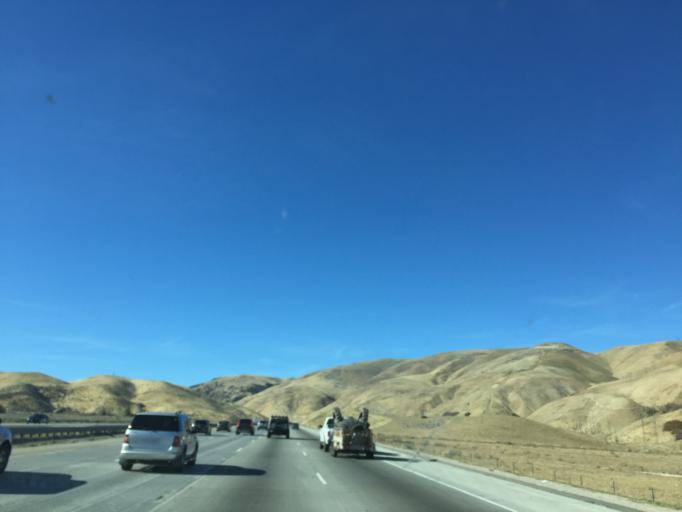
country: US
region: California
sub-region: Kern County
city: Lebec
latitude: 34.7841
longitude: -118.8227
